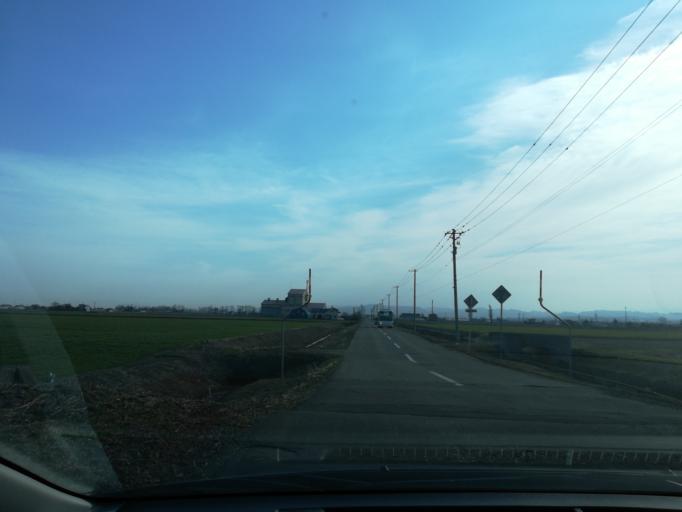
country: JP
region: Hokkaido
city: Iwamizawa
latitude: 43.1922
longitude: 141.7105
